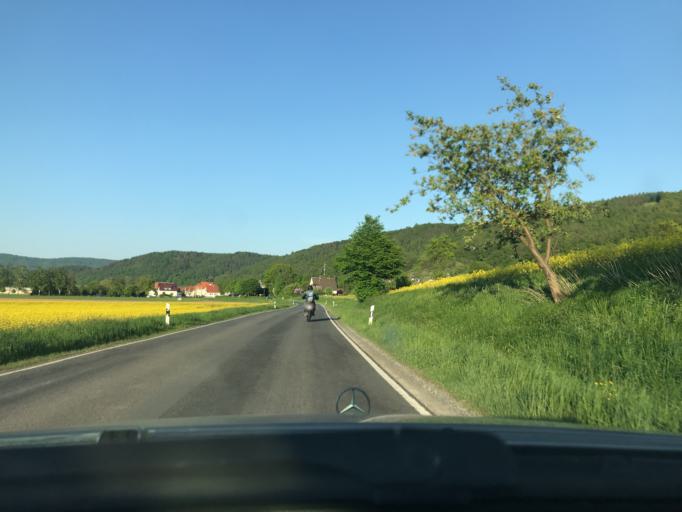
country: DE
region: Hesse
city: Wanfried
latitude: 51.1767
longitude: 10.1152
